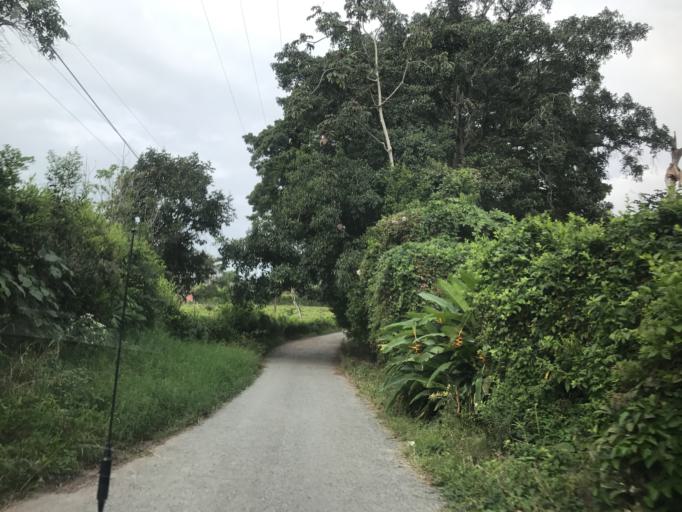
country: CO
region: Quindio
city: Montenegro
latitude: 4.5409
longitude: -75.8554
